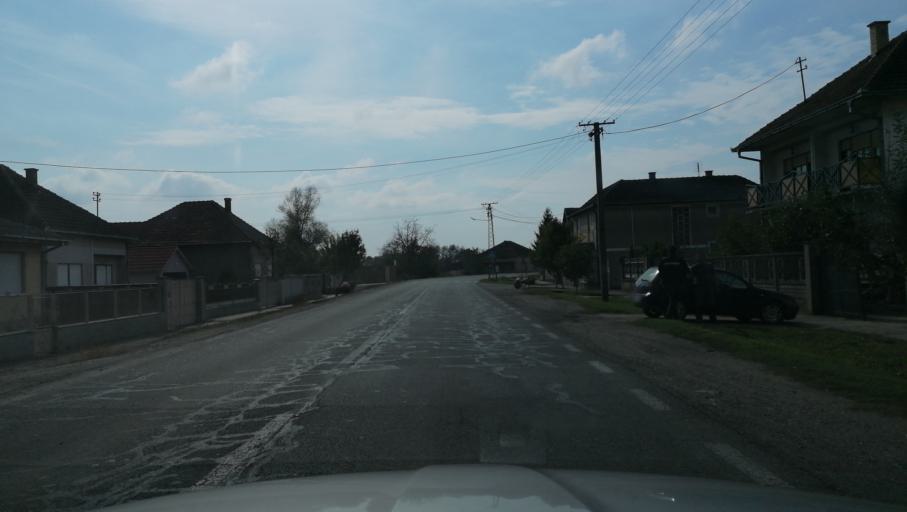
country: RS
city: Ravnje
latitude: 45.0161
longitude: 19.3996
